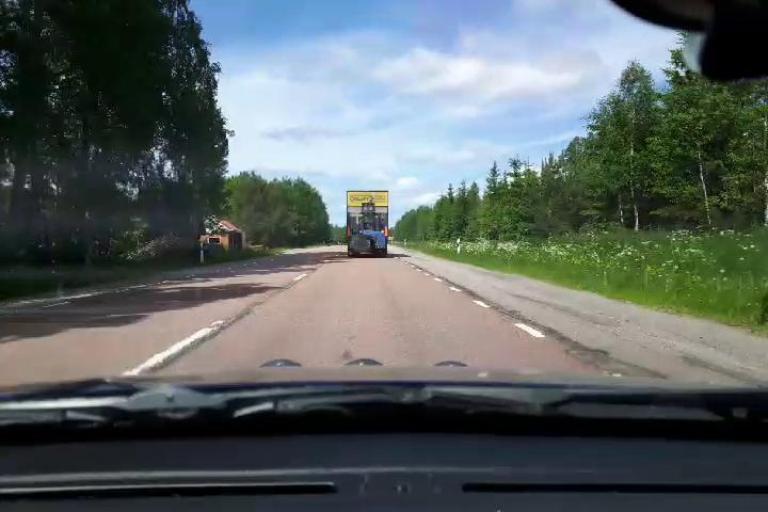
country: SE
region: Uppsala
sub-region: Osthammars Kommun
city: Bjorklinge
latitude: 60.1514
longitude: 17.4930
